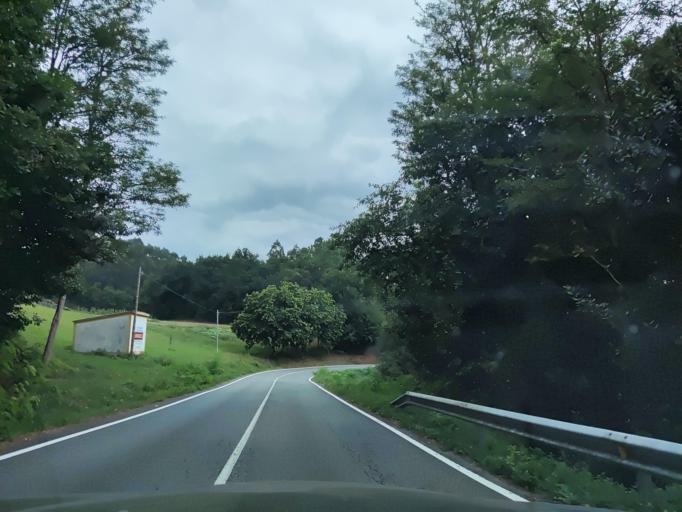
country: ES
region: Galicia
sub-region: Provincia da Coruna
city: Teo
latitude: 42.7579
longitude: -8.5601
